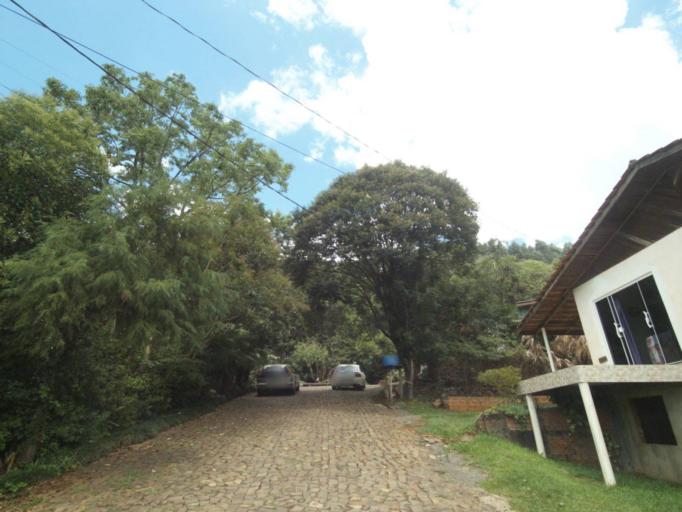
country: BR
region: Parana
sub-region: Pinhao
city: Pinhao
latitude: -26.1591
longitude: -51.5618
